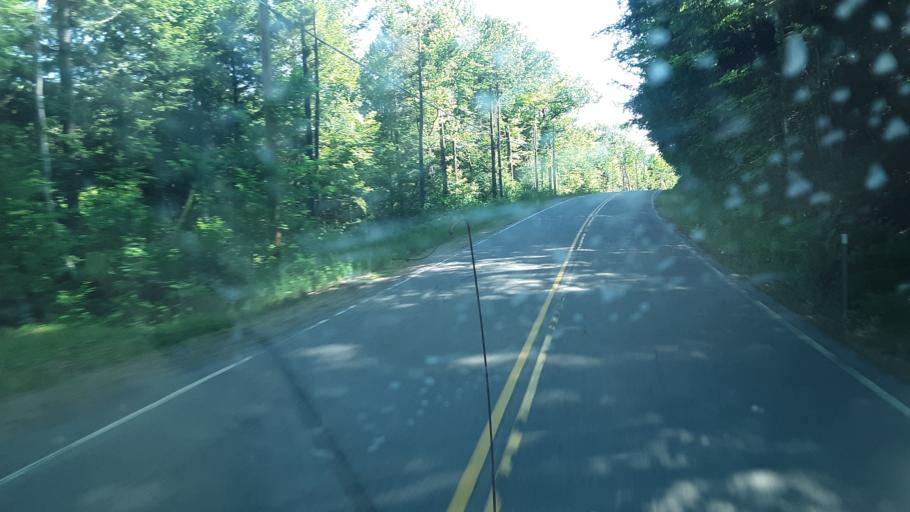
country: US
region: New Hampshire
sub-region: Grafton County
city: North Haverhill
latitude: 44.0786
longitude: -71.9758
